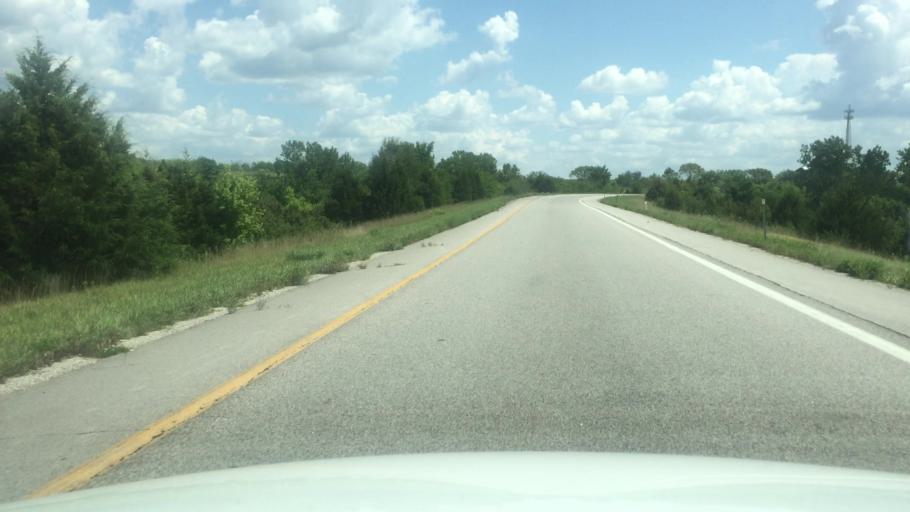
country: US
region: Missouri
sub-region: Platte County
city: Platte City
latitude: 39.3461
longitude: -94.7537
